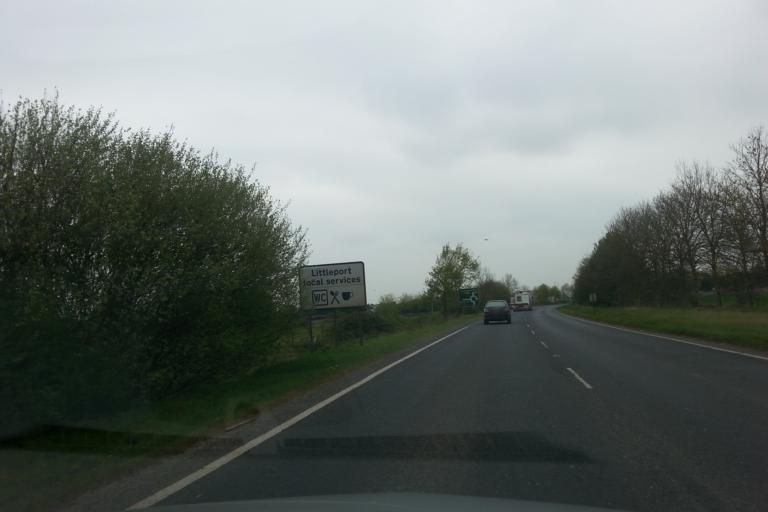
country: GB
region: England
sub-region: Cambridgeshire
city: Littleport
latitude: 52.4593
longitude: 0.2839
